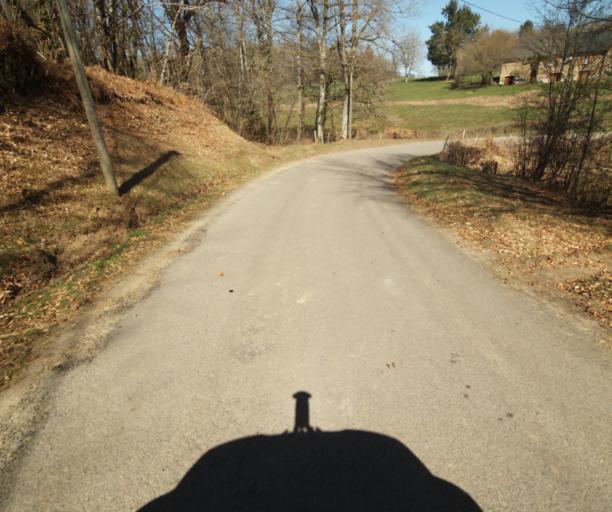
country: FR
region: Limousin
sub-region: Departement de la Correze
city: Saint-Clement
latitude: 45.3060
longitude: 1.7065
